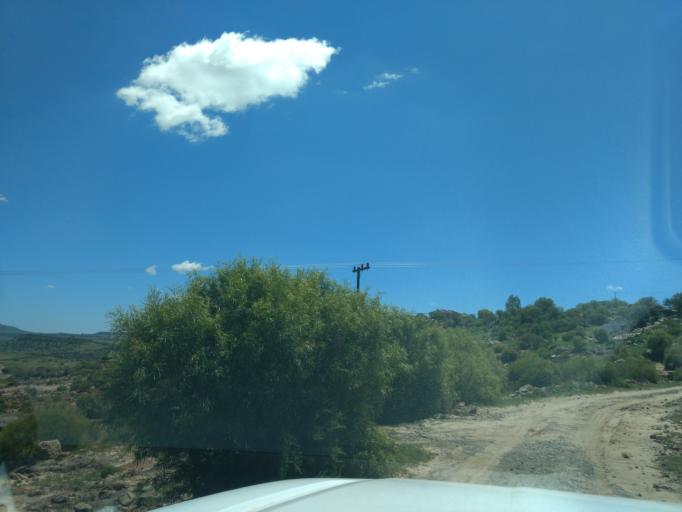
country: LS
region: Maseru
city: Maseru
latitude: -29.4592
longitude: 27.3738
